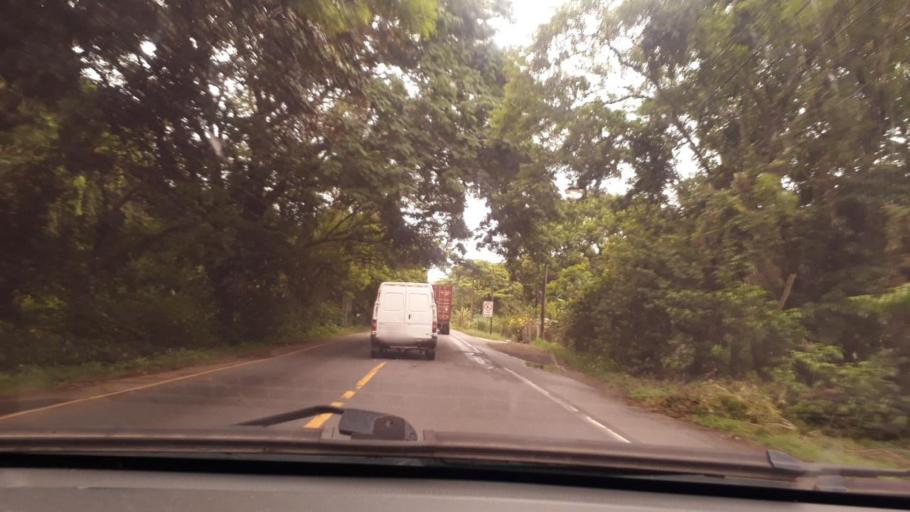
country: GT
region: Izabal
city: Morales
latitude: 15.5386
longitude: -88.7398
